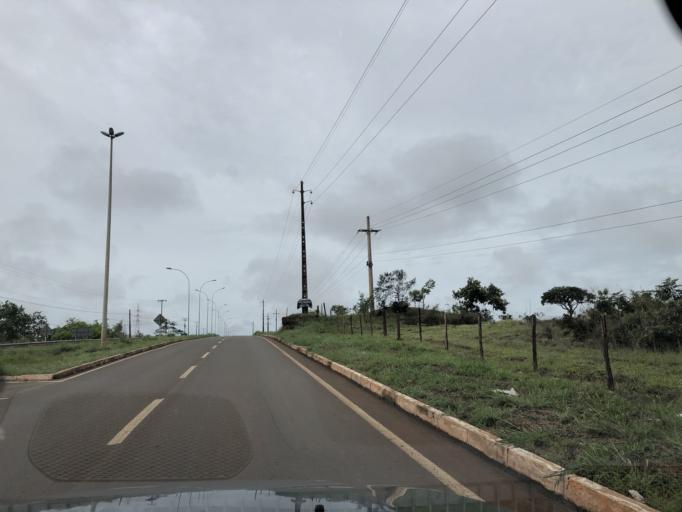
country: BR
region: Federal District
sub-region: Brasilia
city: Brasilia
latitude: -15.7755
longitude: -48.1292
